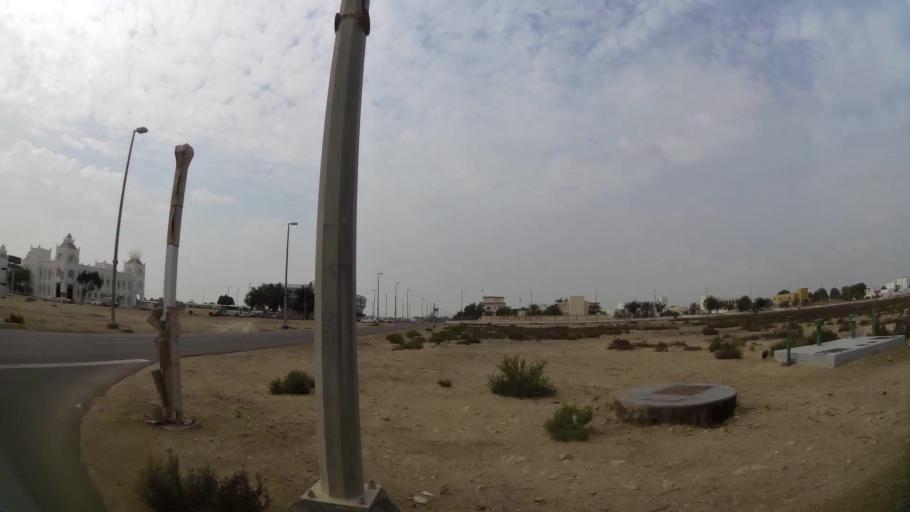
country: AE
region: Abu Dhabi
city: Abu Dhabi
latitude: 24.6384
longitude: 54.7278
